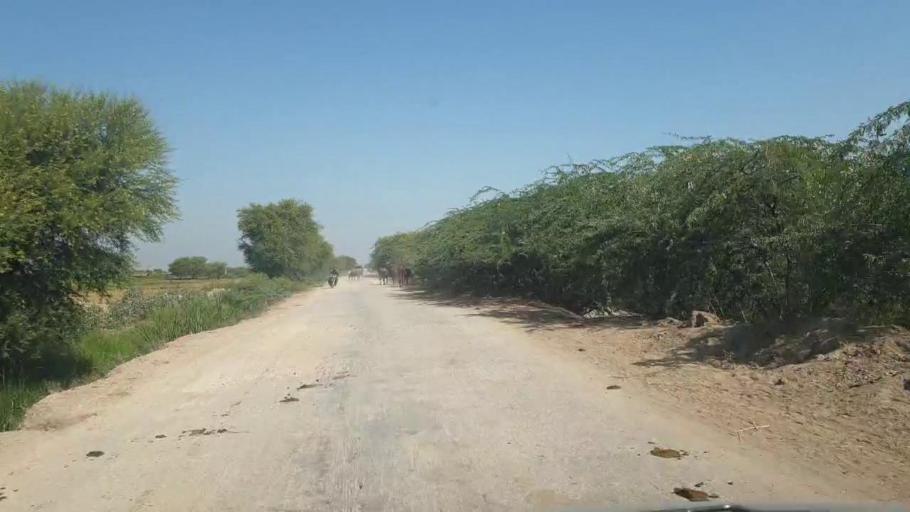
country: PK
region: Sindh
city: Tando Bago
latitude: 24.8012
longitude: 68.9776
